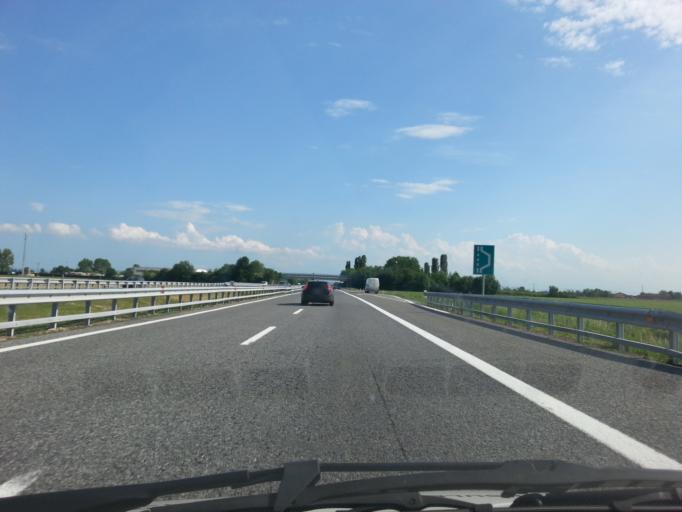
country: IT
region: Piedmont
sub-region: Provincia di Cuneo
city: Caramagna Piemonte
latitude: 44.7458
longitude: 7.7510
